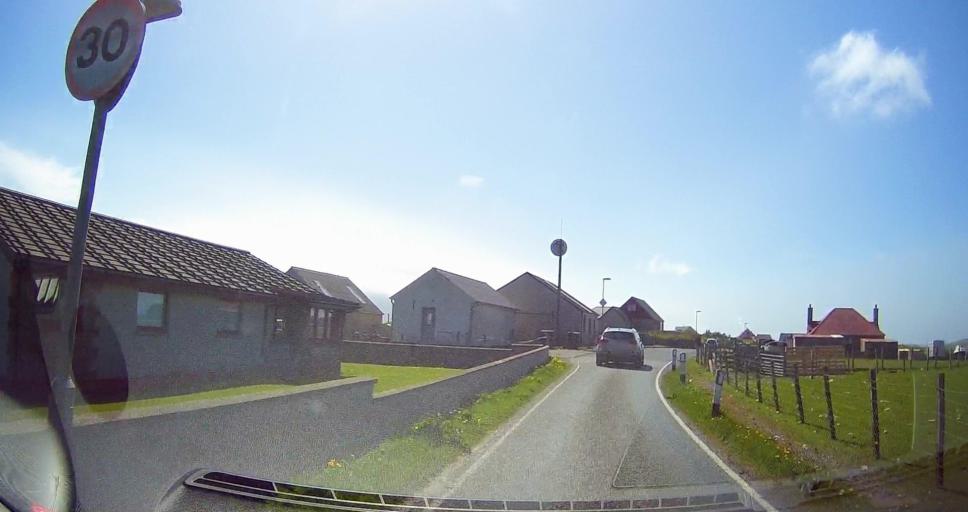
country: GB
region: Scotland
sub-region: Shetland Islands
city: Sandwick
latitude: 60.0986
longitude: -1.3210
